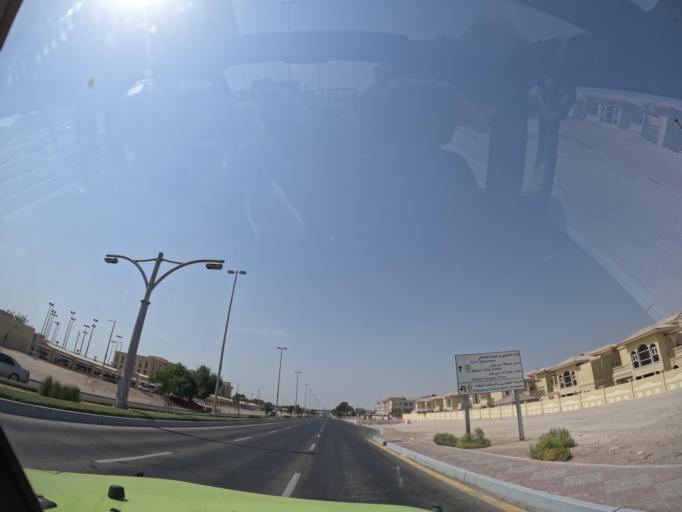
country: AE
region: Abu Dhabi
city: Abu Dhabi
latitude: 24.3055
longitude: 54.6216
